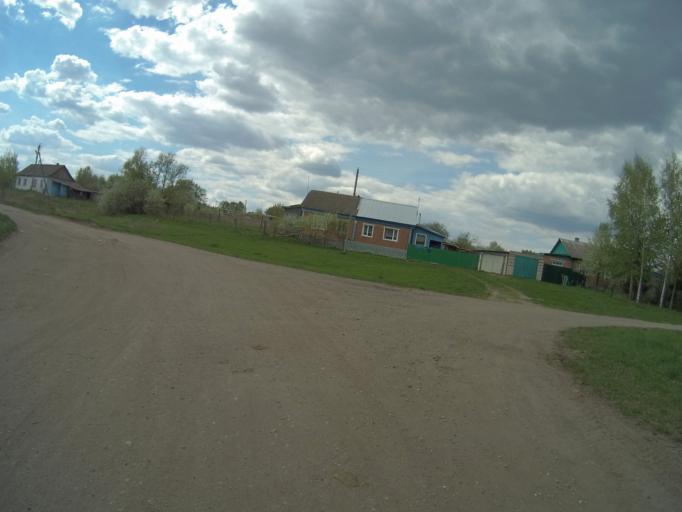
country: RU
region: Vladimir
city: Suzdal'
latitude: 56.3042
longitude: 40.2902
